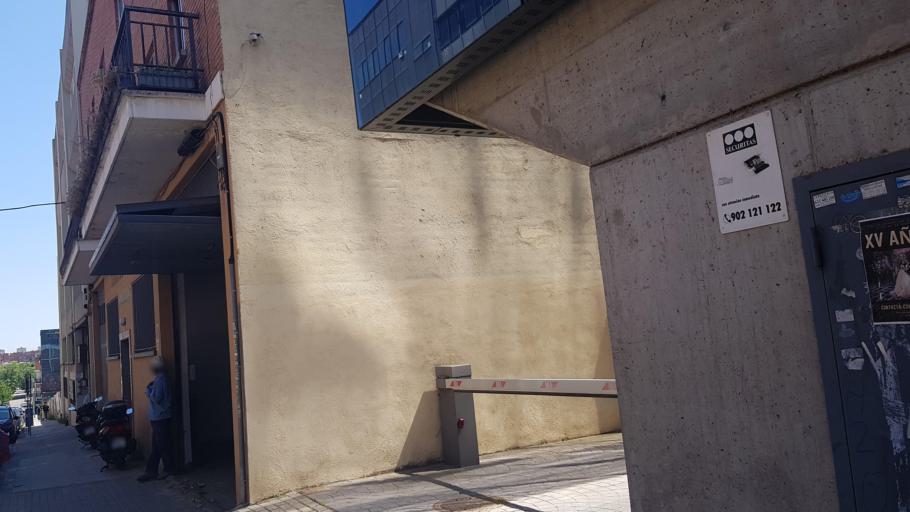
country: ES
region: Madrid
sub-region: Provincia de Madrid
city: San Blas
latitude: 40.4400
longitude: -3.6274
